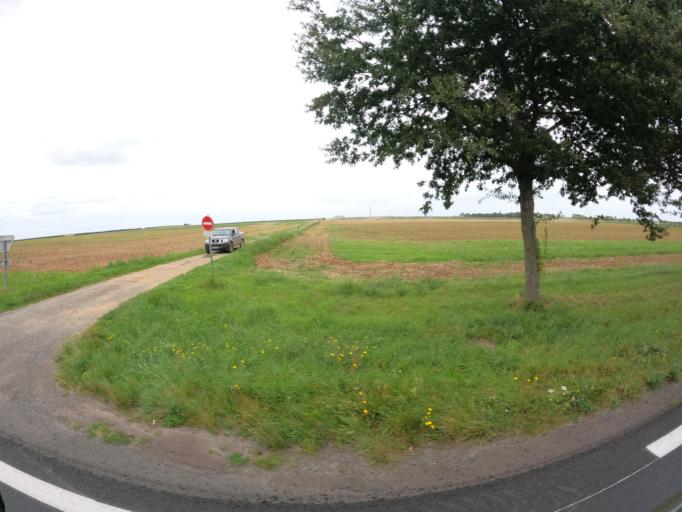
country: FR
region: Pays de la Loire
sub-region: Departement de la Vendee
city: Le Langon
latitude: 46.4927
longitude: -0.9116
